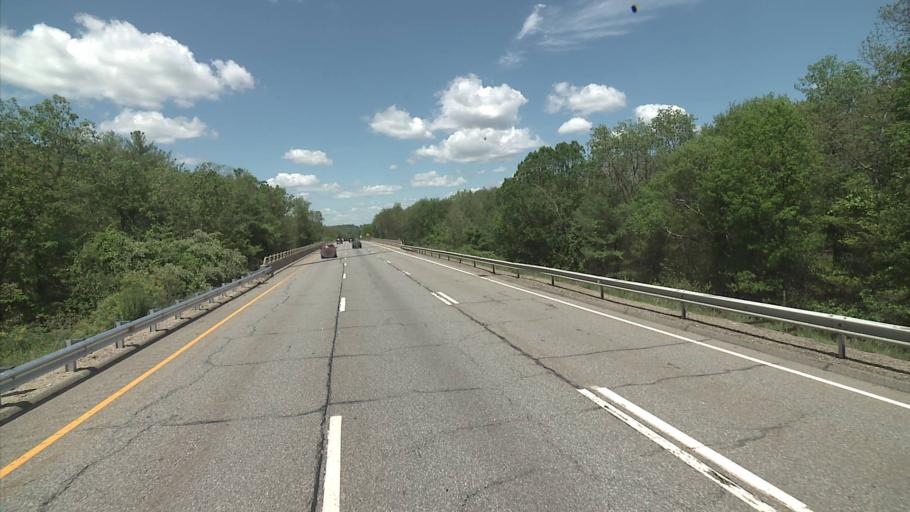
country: US
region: Connecticut
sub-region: Windham County
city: Killingly Center
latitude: 41.8740
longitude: -71.8925
